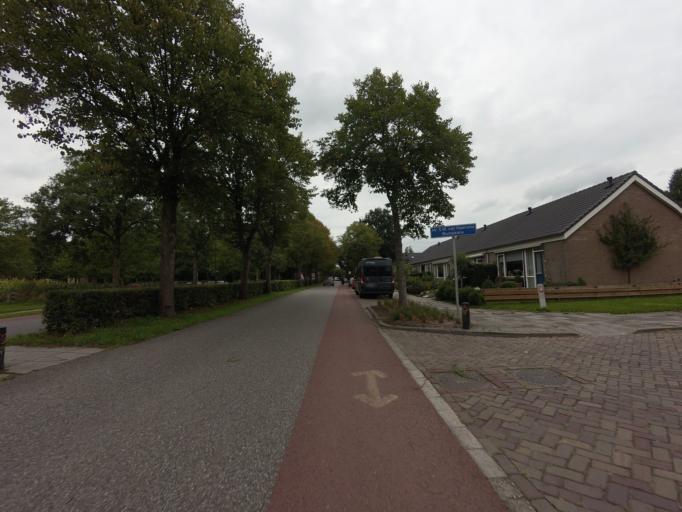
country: NL
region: Friesland
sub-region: Sudwest Fryslan
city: Sneek
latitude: 53.0407
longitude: 5.6351
